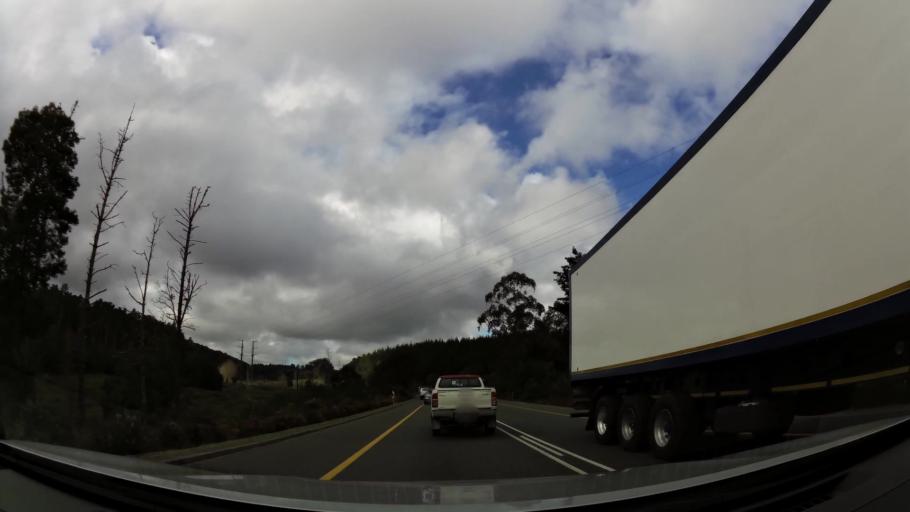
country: ZA
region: Western Cape
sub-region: Eden District Municipality
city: Knysna
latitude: -34.0308
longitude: 23.1872
